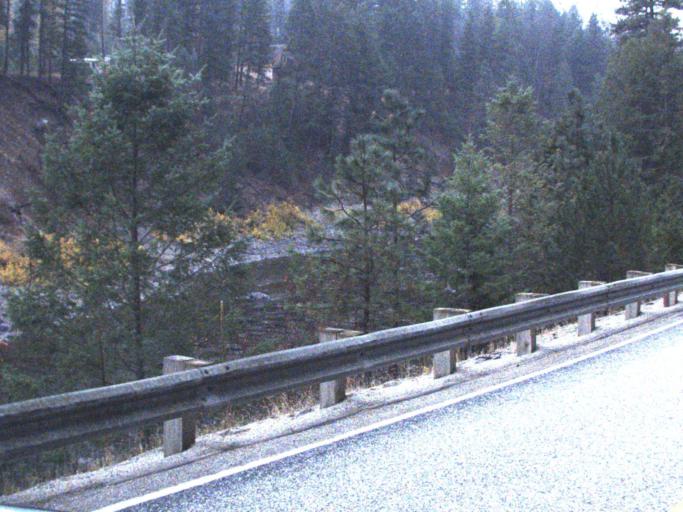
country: CA
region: British Columbia
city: Grand Forks
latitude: 48.9365
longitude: -118.2221
